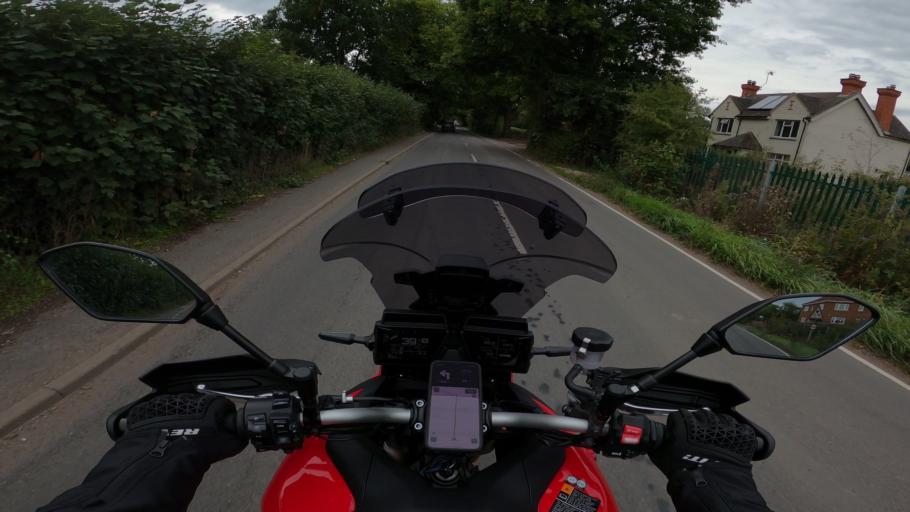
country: GB
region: England
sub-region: Surrey
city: Lingfield
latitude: 51.1855
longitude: -0.0156
